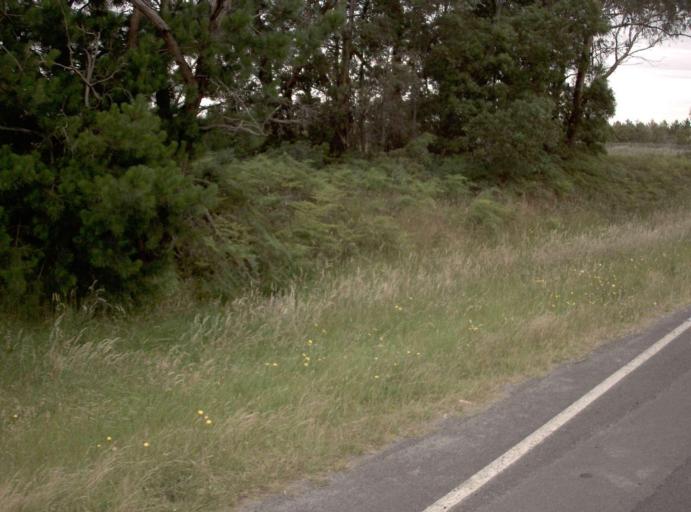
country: AU
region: Victoria
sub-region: Casey
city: Junction Village
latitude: -38.1342
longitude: 145.2980
